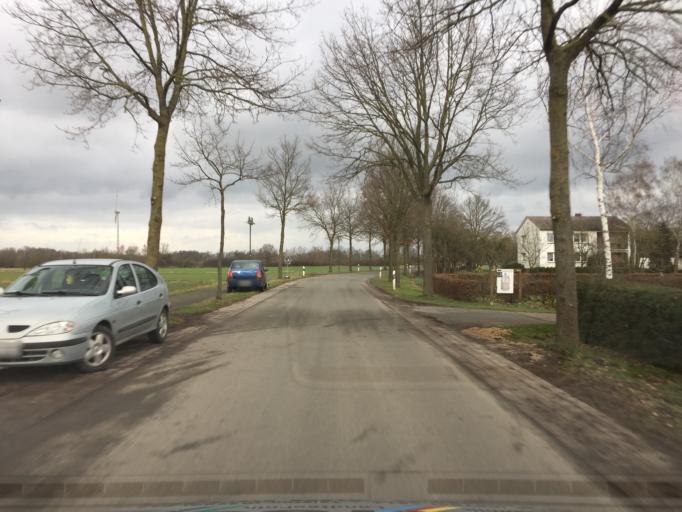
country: DE
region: Lower Saxony
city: Stolzenau
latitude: 52.4856
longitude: 9.0642
